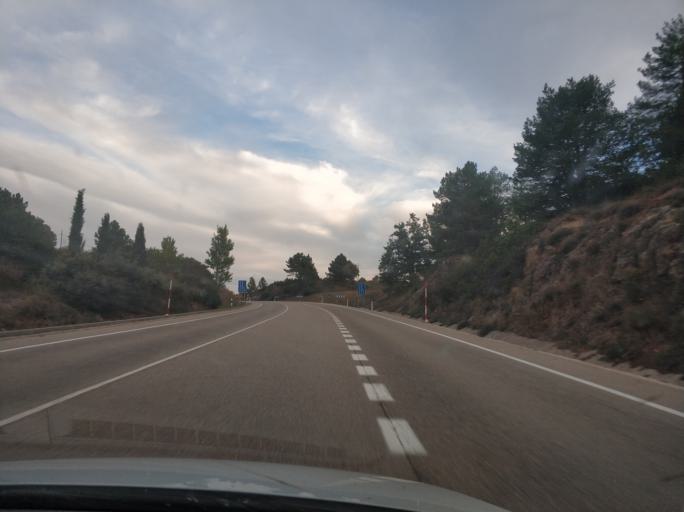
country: ES
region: Castille and Leon
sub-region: Provincia de Burgos
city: Pinilla de los Barruecos
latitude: 41.9003
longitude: -3.2711
